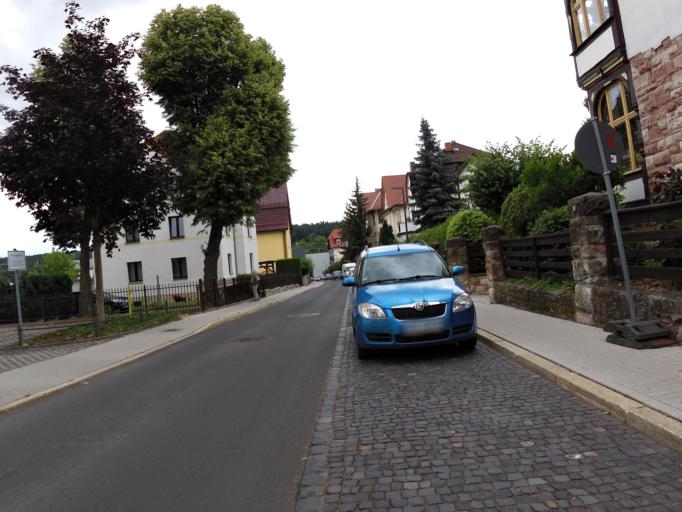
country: DE
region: Thuringia
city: Bad Salzungen
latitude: 50.8128
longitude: 10.2285
